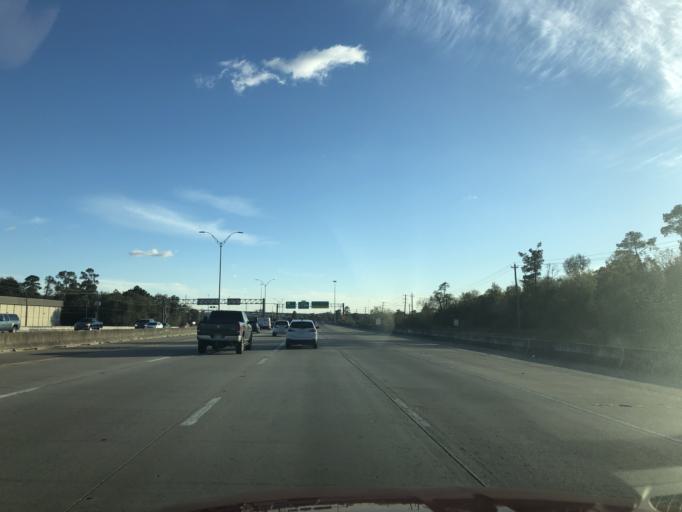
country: US
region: Texas
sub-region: Harris County
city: Cloverleaf
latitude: 29.7828
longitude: -95.1587
